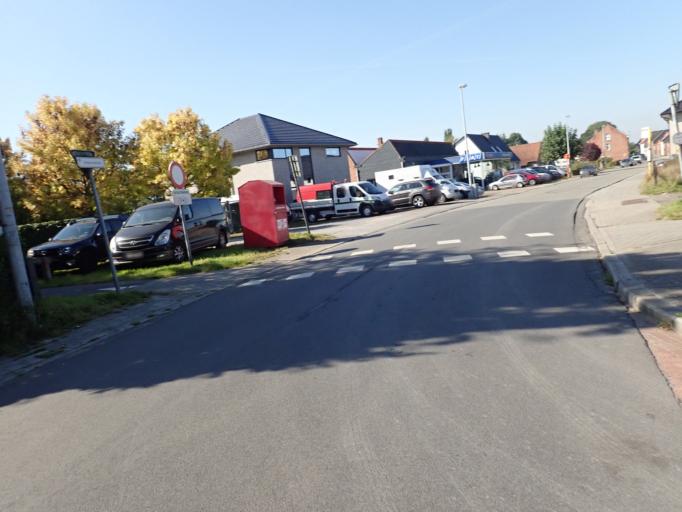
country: BE
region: Flanders
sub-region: Provincie Oost-Vlaanderen
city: Sint-Gillis-Waas
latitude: 51.2179
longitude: 4.1136
